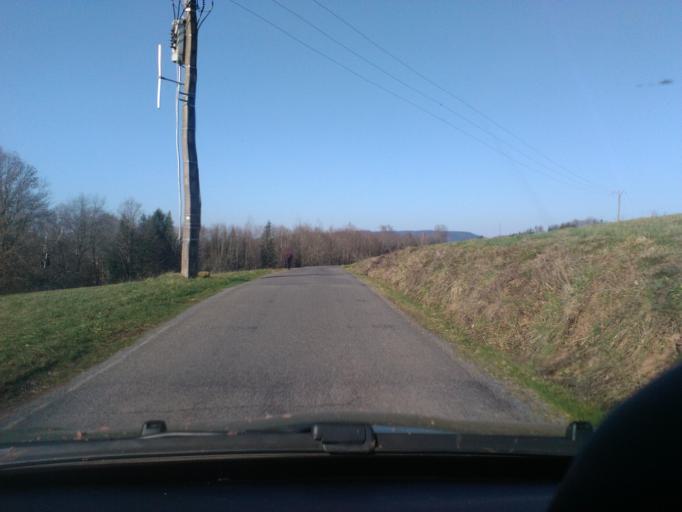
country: FR
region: Lorraine
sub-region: Departement des Vosges
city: Moyenmoutier
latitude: 48.3594
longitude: 6.9228
